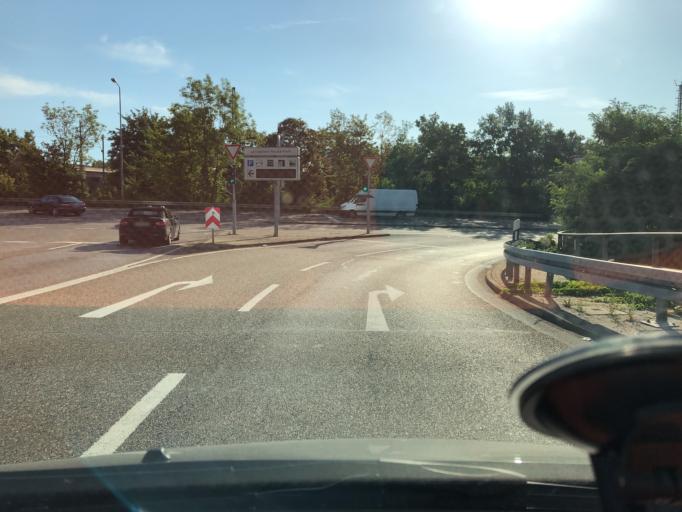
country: DE
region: Baden-Wuerttemberg
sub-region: Regierungsbezirk Stuttgart
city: Stuttgart-Ost
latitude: 48.7890
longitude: 9.2420
